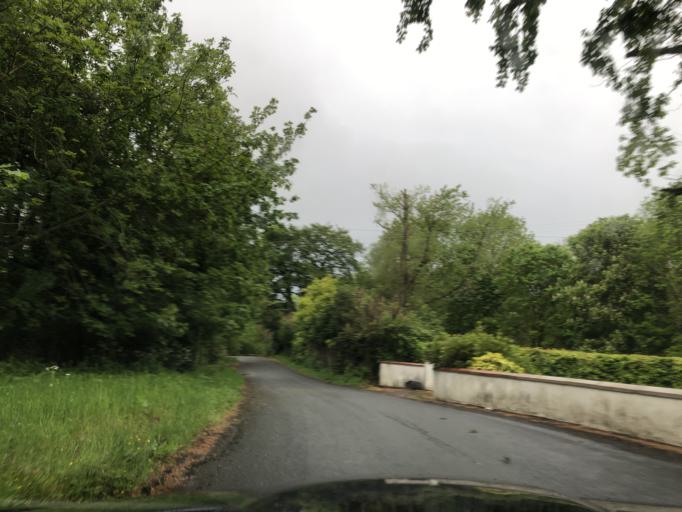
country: GB
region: Northern Ireland
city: Dunloy
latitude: 55.1400
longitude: -6.3776
